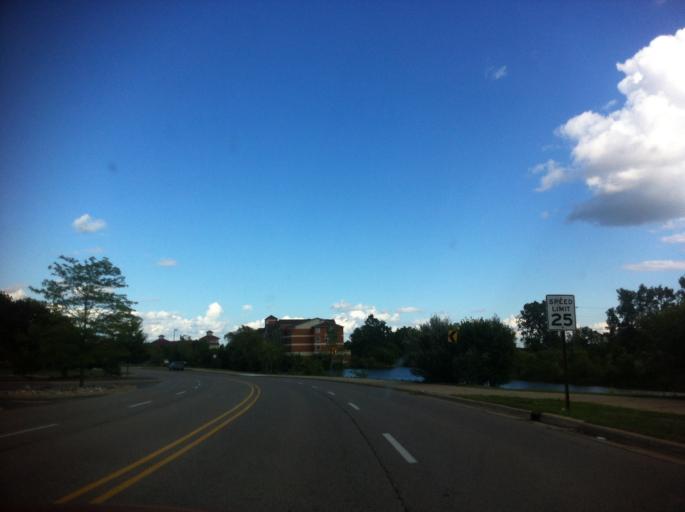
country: US
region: Michigan
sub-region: Washtenaw County
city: Ann Arbor
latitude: 42.2377
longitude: -83.7456
